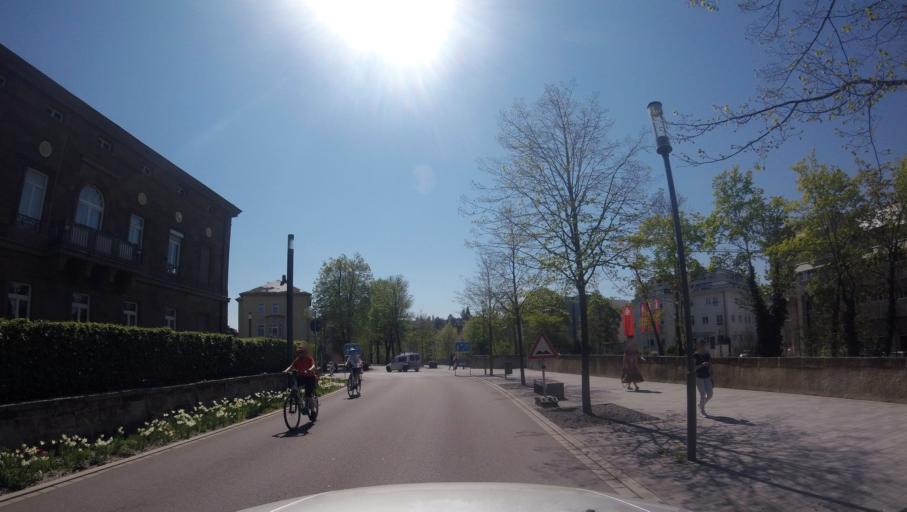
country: DE
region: Baden-Wuerttemberg
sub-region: Regierungsbezirk Stuttgart
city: Schwabisch Gmund
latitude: 48.7989
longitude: 9.7922
